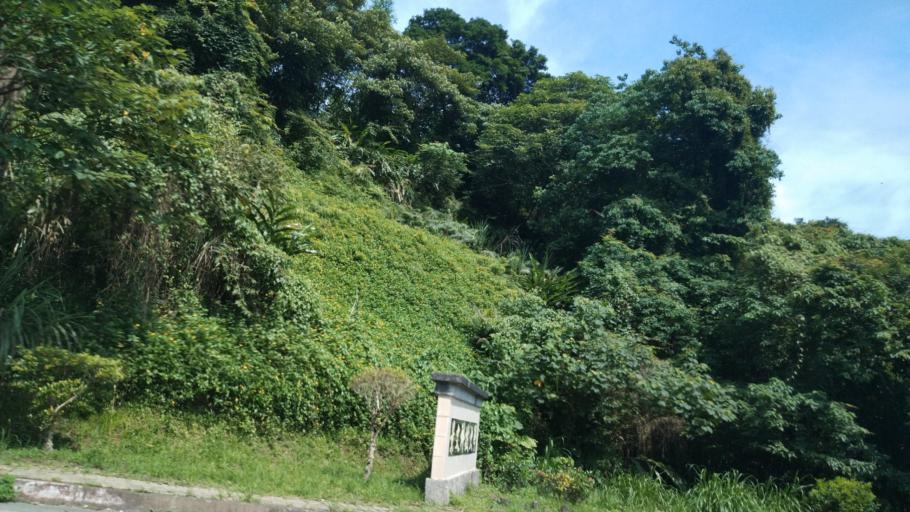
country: TW
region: Taipei
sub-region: Taipei
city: Banqiao
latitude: 24.9539
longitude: 121.5091
